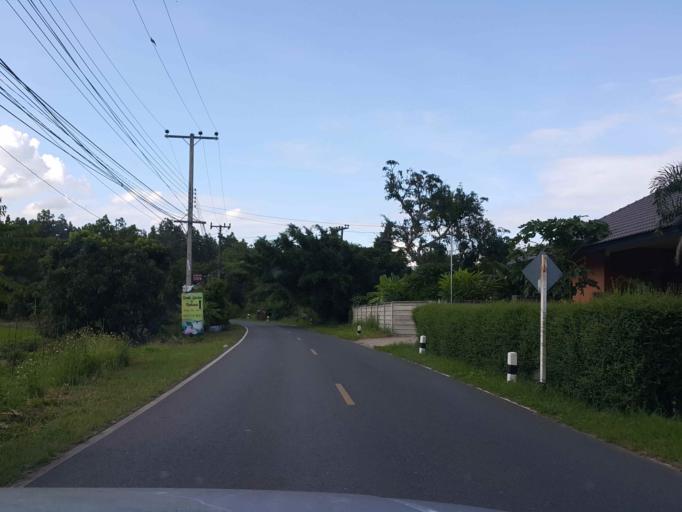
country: TH
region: Chiang Mai
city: Mae Taeng
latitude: 18.9620
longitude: 98.9221
